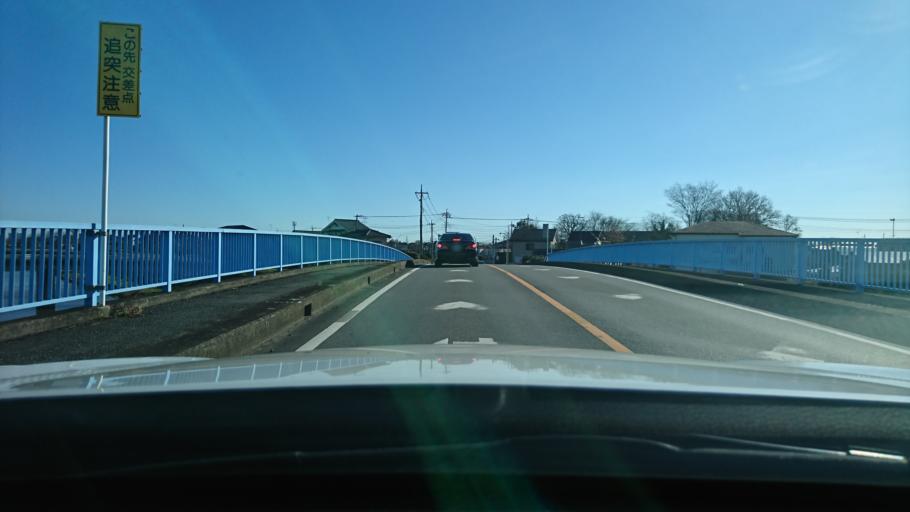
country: JP
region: Saitama
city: Kamifukuoka
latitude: 35.8826
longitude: 139.5471
